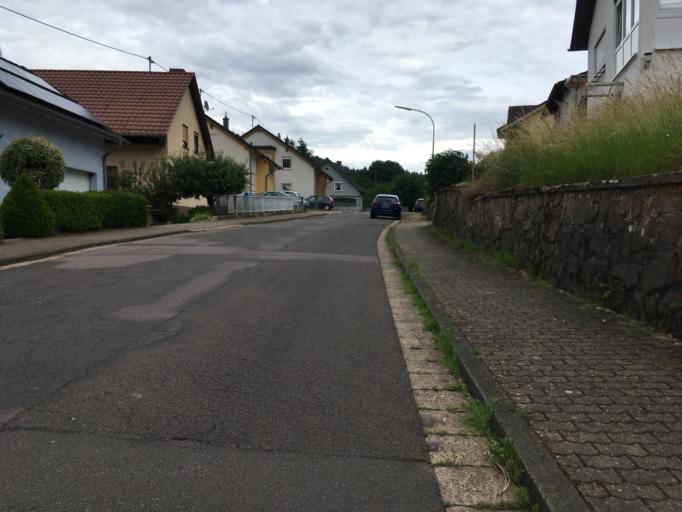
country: DE
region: Saarland
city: Mettlach
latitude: 49.4920
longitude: 6.6102
